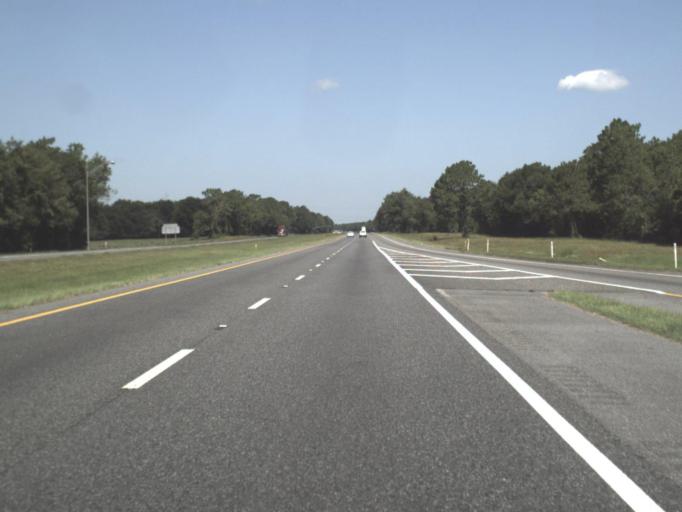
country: US
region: Florida
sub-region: Suwannee County
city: Live Oak
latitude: 30.3504
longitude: -83.1578
